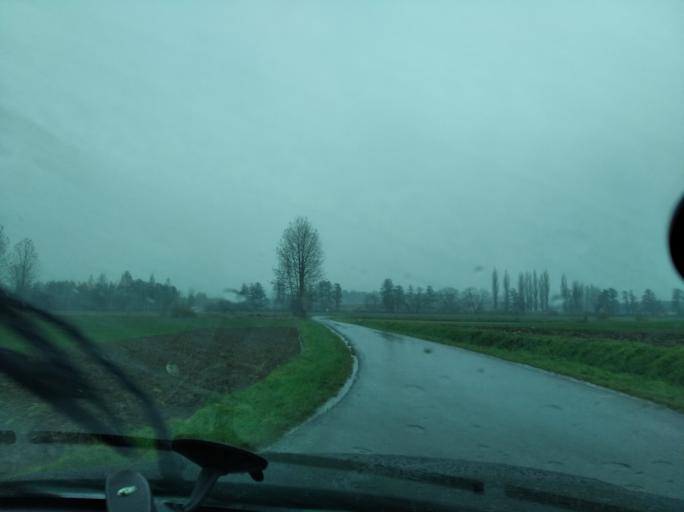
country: PL
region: Subcarpathian Voivodeship
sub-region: Powiat lancucki
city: Albigowa
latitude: 50.0381
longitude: 22.2171
